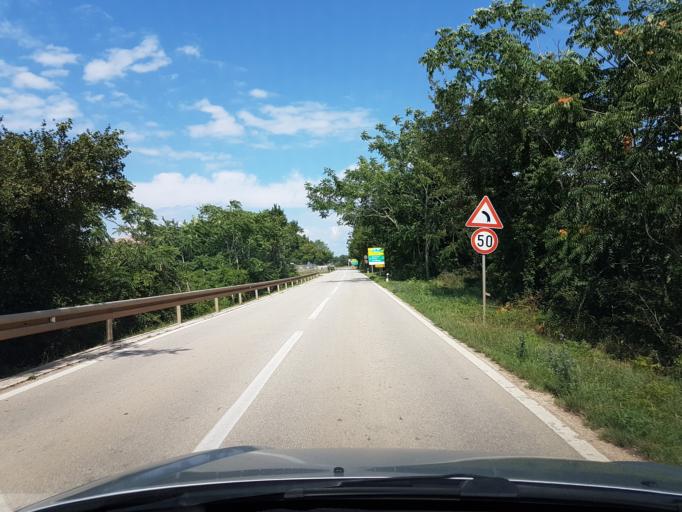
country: HR
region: Istarska
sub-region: Grad Rovinj
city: Rovinj
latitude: 45.1484
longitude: 13.7365
